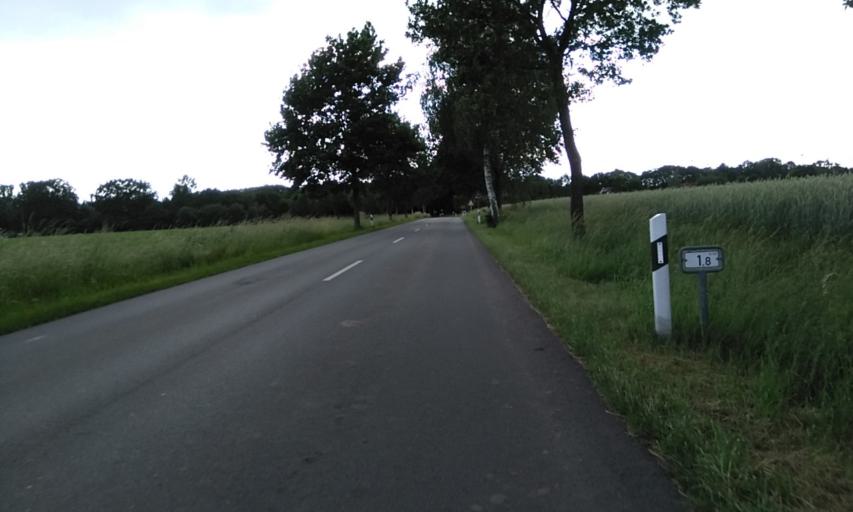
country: DE
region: Lower Saxony
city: Wohnste
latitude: 53.3583
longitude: 9.5493
